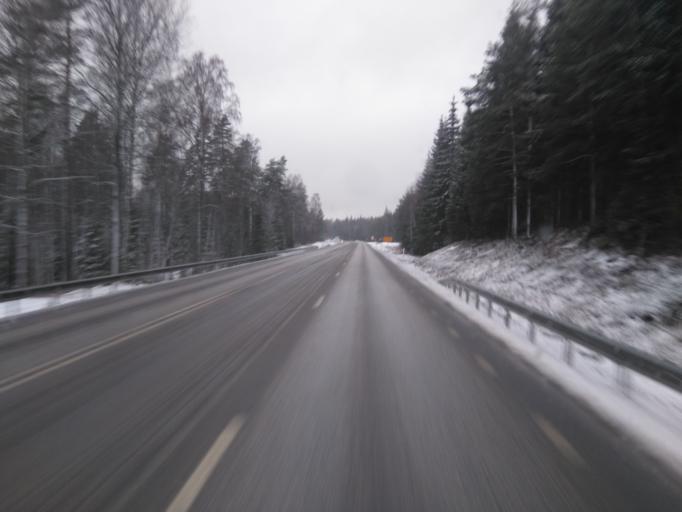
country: SE
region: Joenkoeping
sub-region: Eksjo Kommun
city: Eksjoe
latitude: 57.6464
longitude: 15.0585
